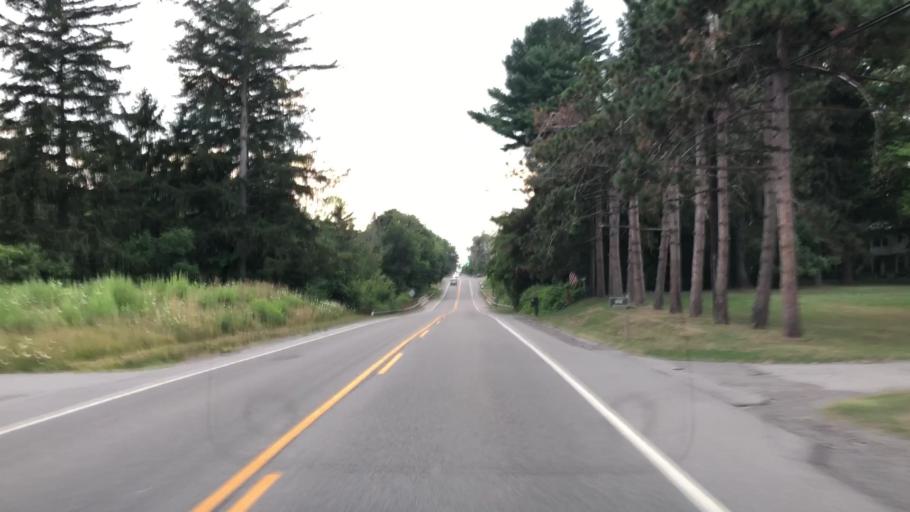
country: US
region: New York
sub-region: Erie County
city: Elma Center
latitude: 42.8393
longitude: -78.6333
